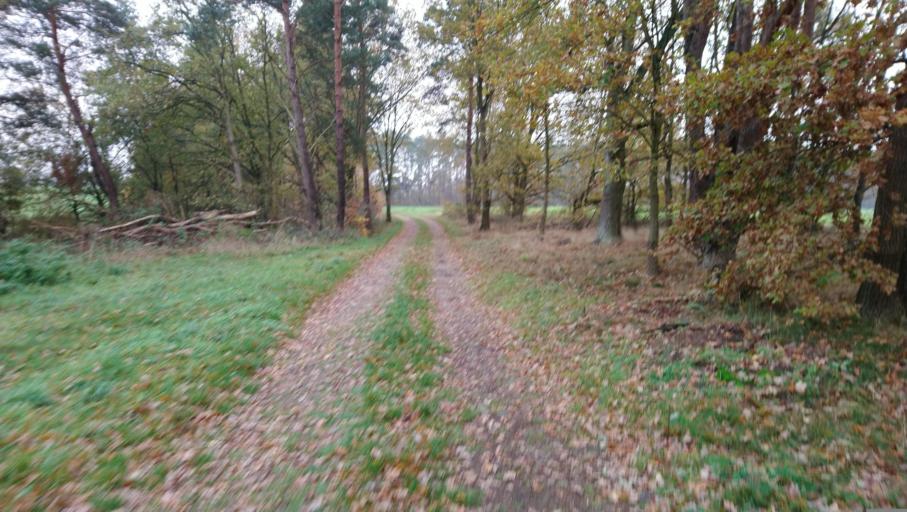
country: DE
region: Lower Saxony
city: Altenmedingen
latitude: 53.1662
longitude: 10.6359
